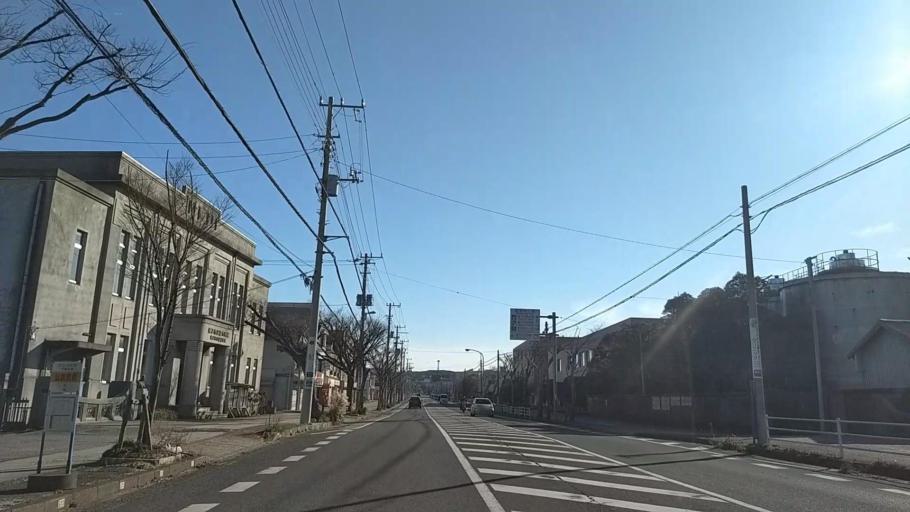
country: JP
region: Chiba
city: Hasaki
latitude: 35.7320
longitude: 140.8327
